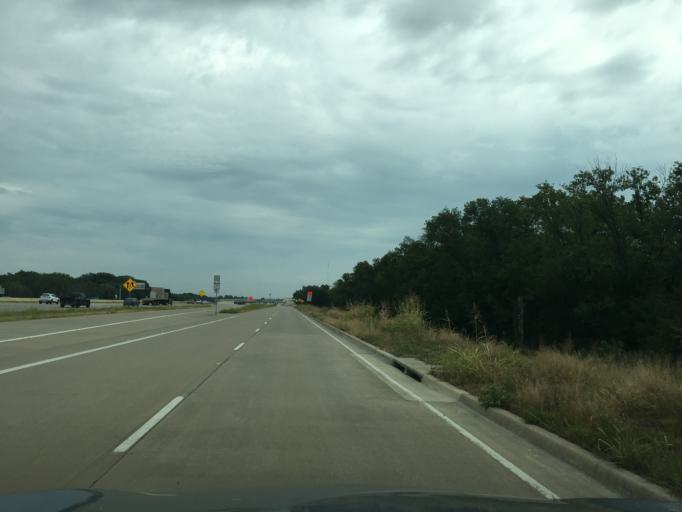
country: US
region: Texas
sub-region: Collin County
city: Melissa
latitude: 33.2539
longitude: -96.6131
